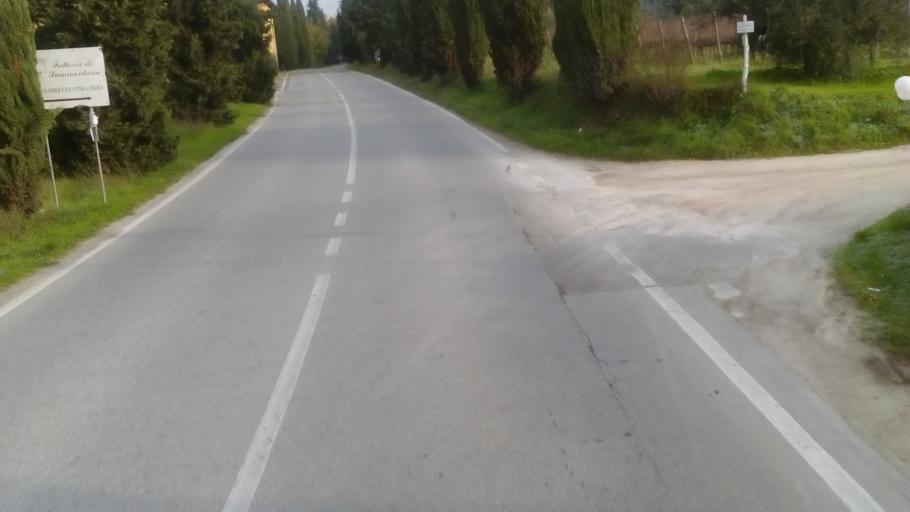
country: IT
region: Tuscany
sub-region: Province of Florence
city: Montelupo Fiorentino
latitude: 43.7153
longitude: 11.0044
